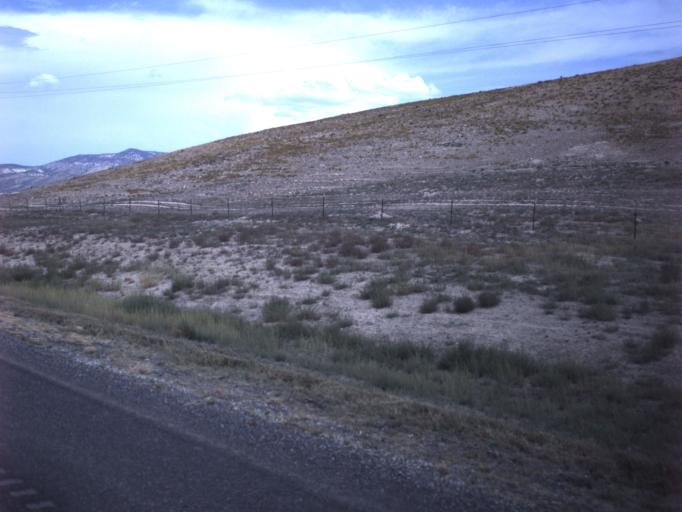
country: US
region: Utah
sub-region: Sanpete County
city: Gunnison
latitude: 39.2023
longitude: -111.8468
